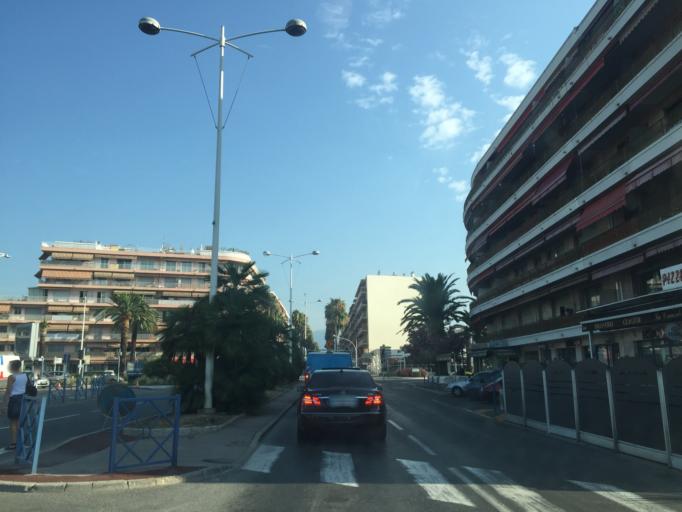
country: FR
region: Provence-Alpes-Cote d'Azur
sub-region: Departement des Alpes-Maritimes
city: Cagnes-sur-Mer
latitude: 43.6544
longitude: 7.1516
